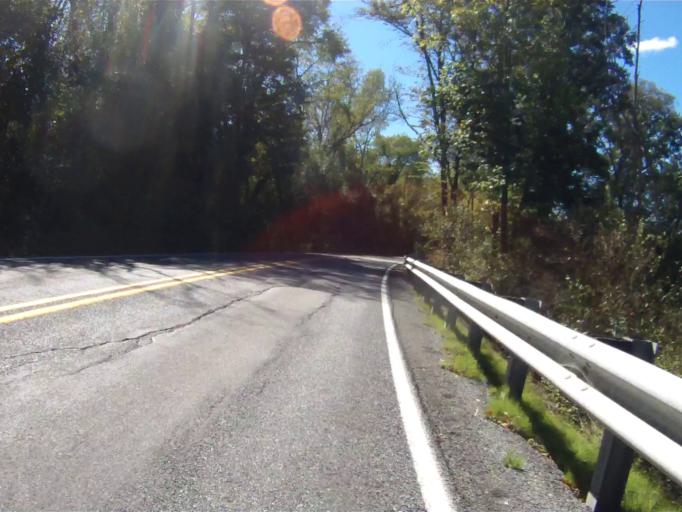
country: US
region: Pennsylvania
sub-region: Centre County
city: Houserville
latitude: 40.8559
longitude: -77.8796
